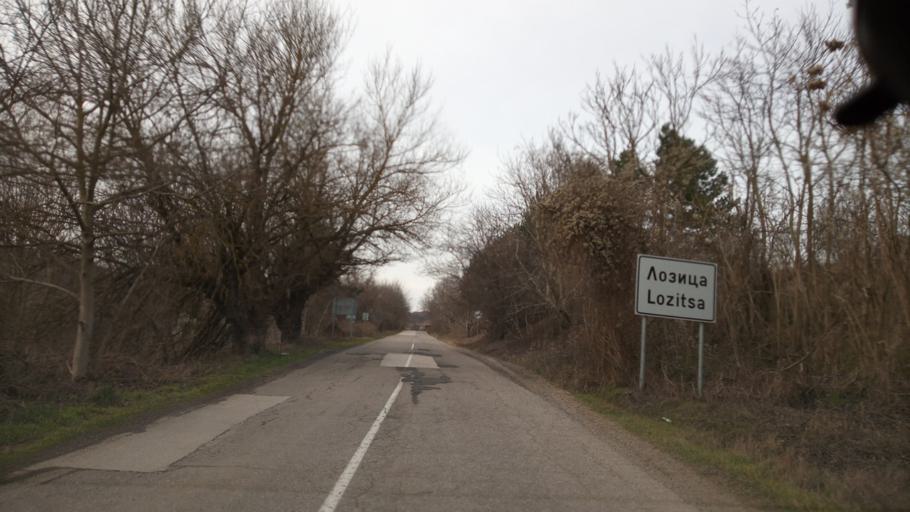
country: BG
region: Pleven
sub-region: Obshtina Belene
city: Belene
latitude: 43.6121
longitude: 25.0187
